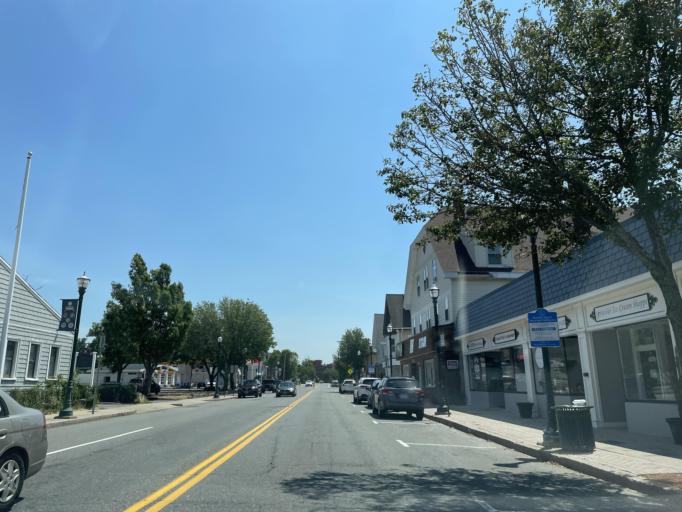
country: US
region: Massachusetts
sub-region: Norfolk County
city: Braintree
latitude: 42.2205
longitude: -71.0040
